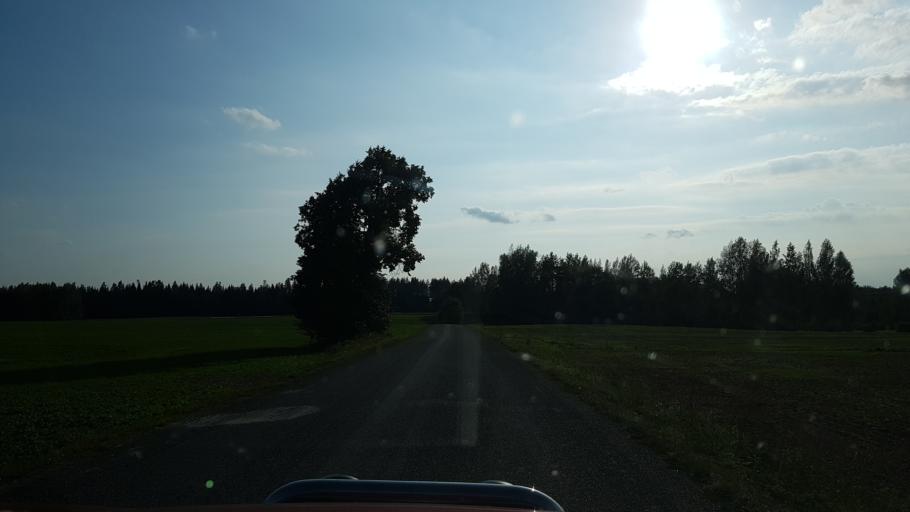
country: EE
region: Polvamaa
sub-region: Polva linn
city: Polva
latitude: 58.1234
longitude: 26.9634
